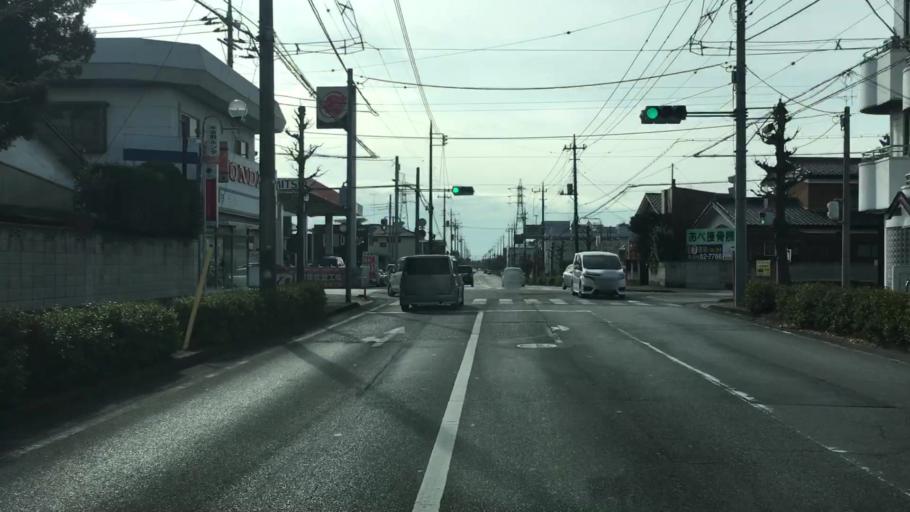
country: JP
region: Saitama
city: Menuma
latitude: 36.2411
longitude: 139.4082
